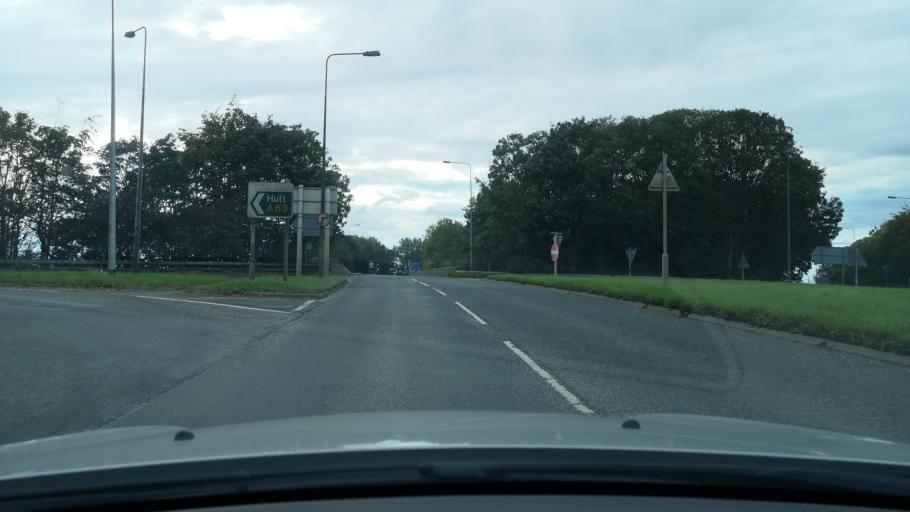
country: GB
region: England
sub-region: East Riding of Yorkshire
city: Newport
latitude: 53.7715
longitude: -0.6755
